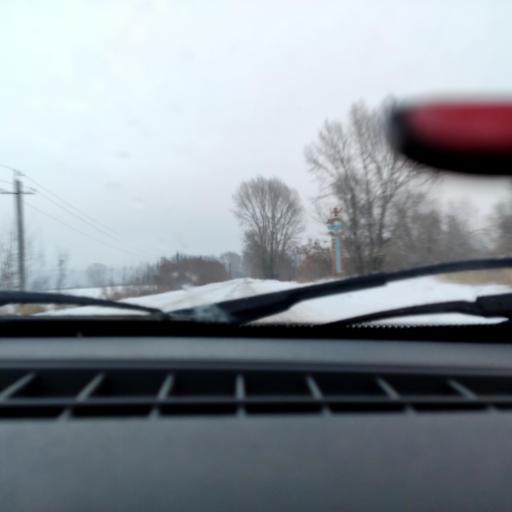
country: RU
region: Bashkortostan
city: Blagoveshchensk
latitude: 54.9117
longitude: 55.9986
